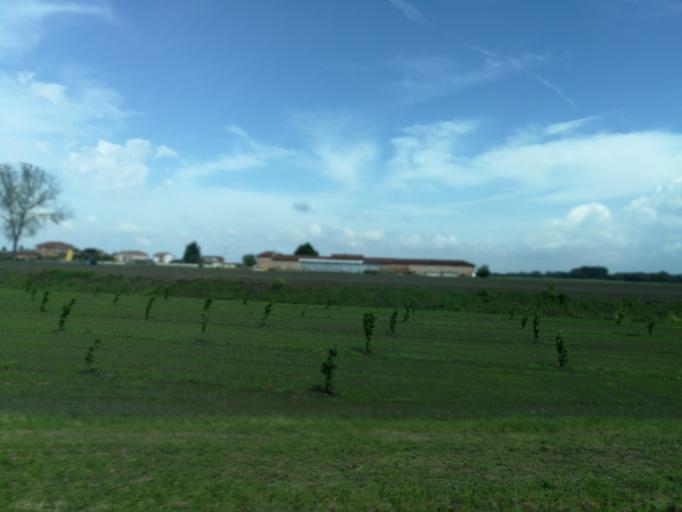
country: IT
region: Piedmont
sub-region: Provincia di Torino
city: Pancalieri
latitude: 44.8269
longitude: 7.5869
